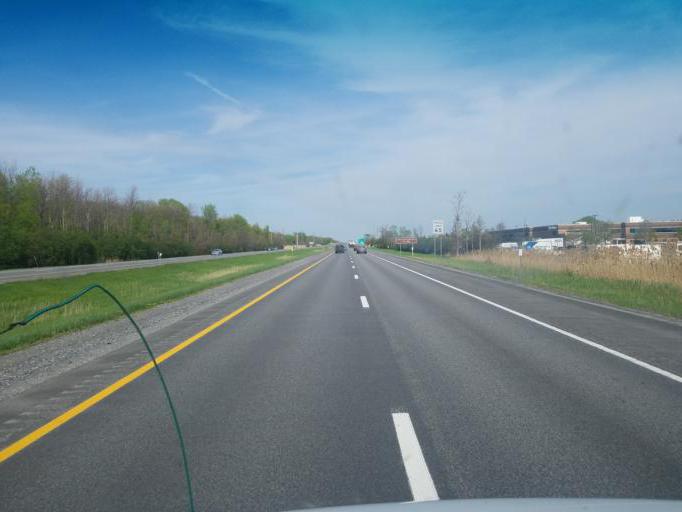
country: US
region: New York
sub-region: Onondaga County
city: East Syracuse
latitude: 43.0939
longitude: -76.0753
